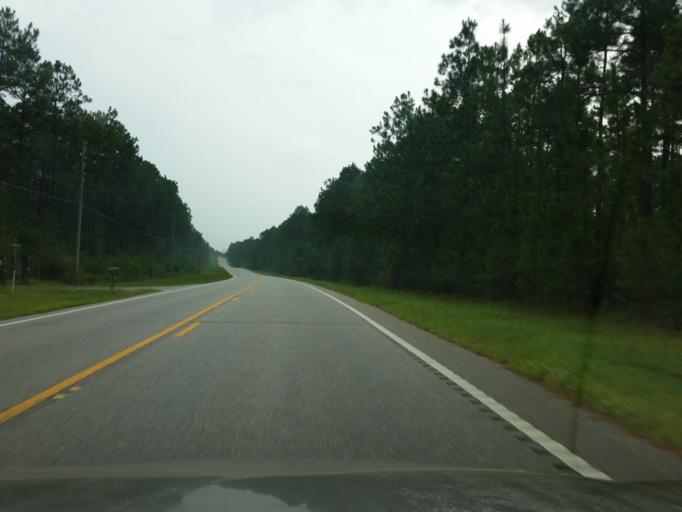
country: US
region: Alabama
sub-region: Baldwin County
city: Elberta
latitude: 30.5244
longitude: -87.4982
